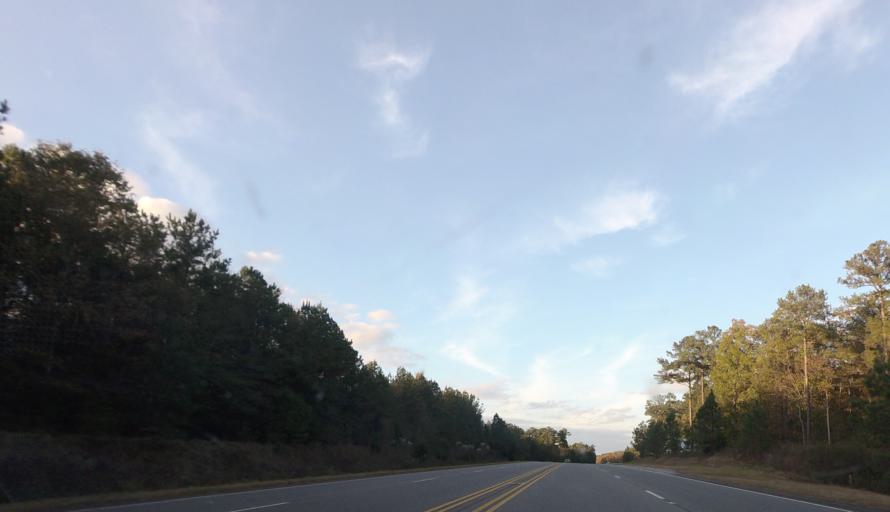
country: US
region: Georgia
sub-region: Houston County
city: Robins Air Force Base
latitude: 32.5352
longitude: -83.4405
